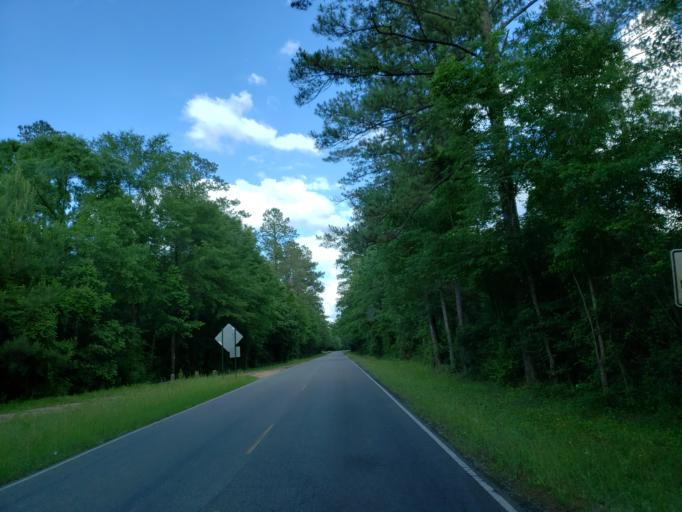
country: US
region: Mississippi
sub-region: Forrest County
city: Petal
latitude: 31.3106
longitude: -89.2321
